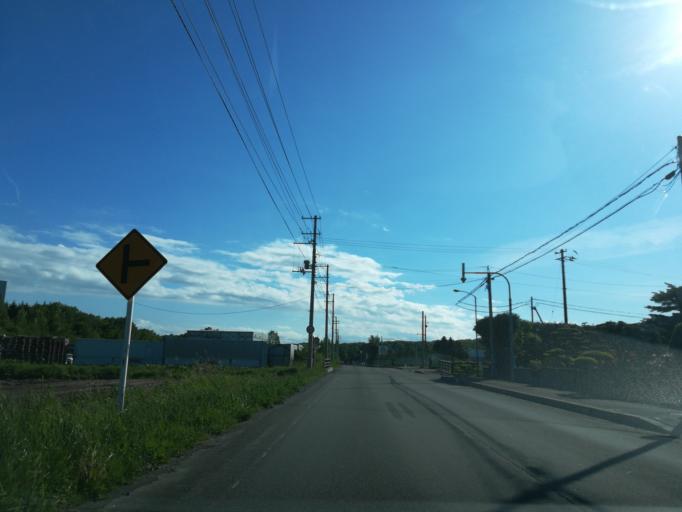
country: JP
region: Hokkaido
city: Kitahiroshima
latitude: 43.0070
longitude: 141.5544
